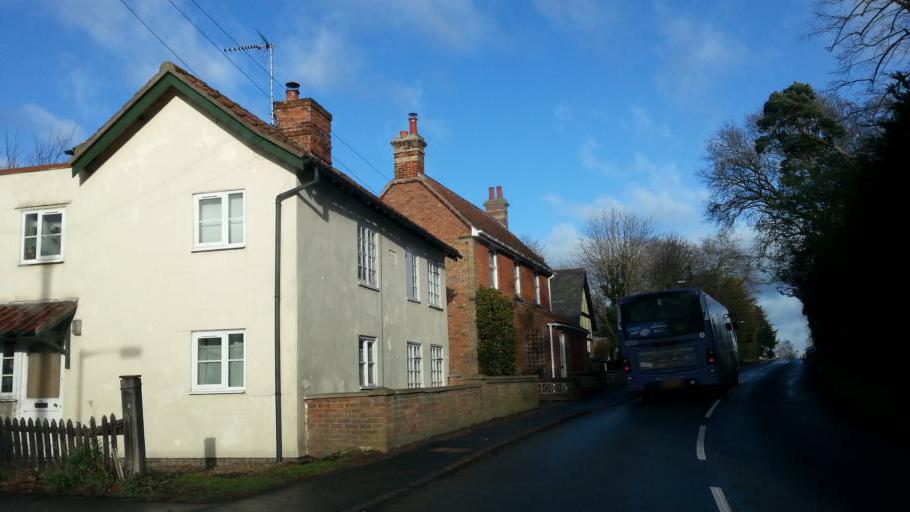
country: GB
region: England
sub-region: Norfolk
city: Ditchingham
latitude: 52.4660
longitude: 1.4417
